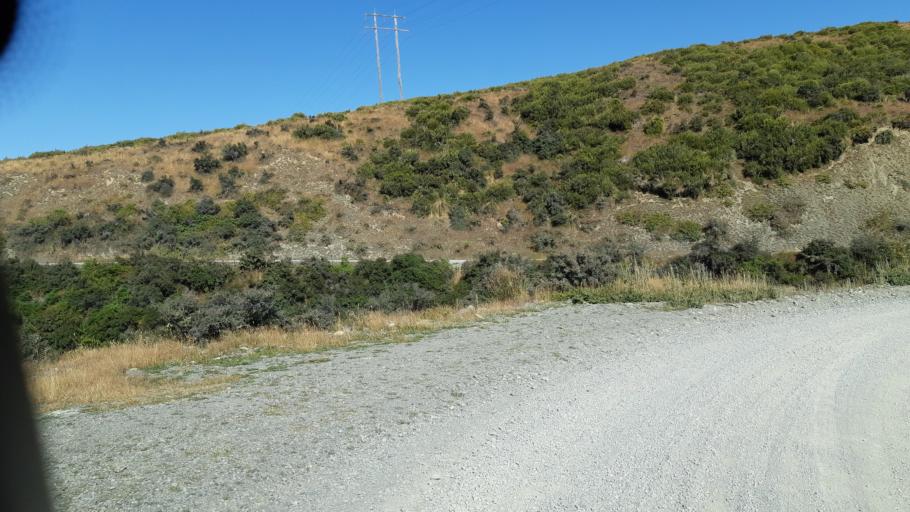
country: NZ
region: Canterbury
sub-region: Ashburton District
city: Methven
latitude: -43.3377
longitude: 171.6495
